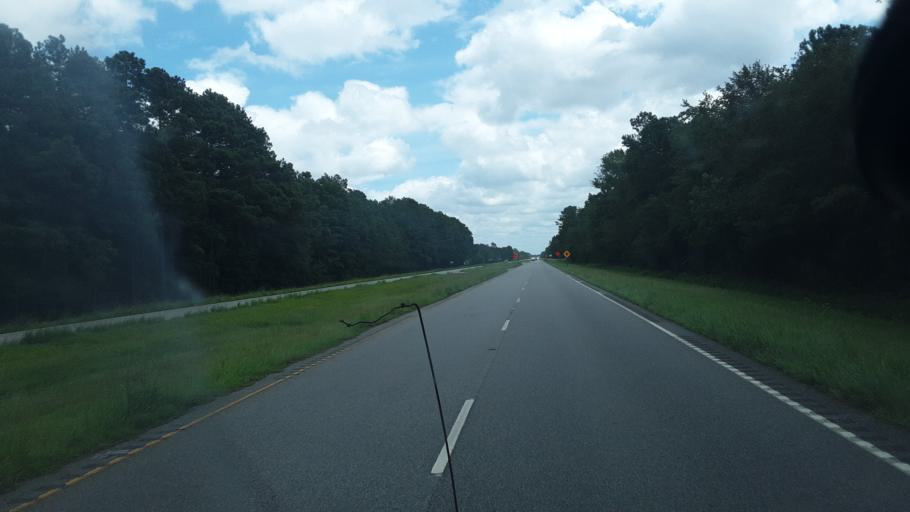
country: US
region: South Carolina
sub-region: Horry County
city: Loris
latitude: 34.0947
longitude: -78.9120
